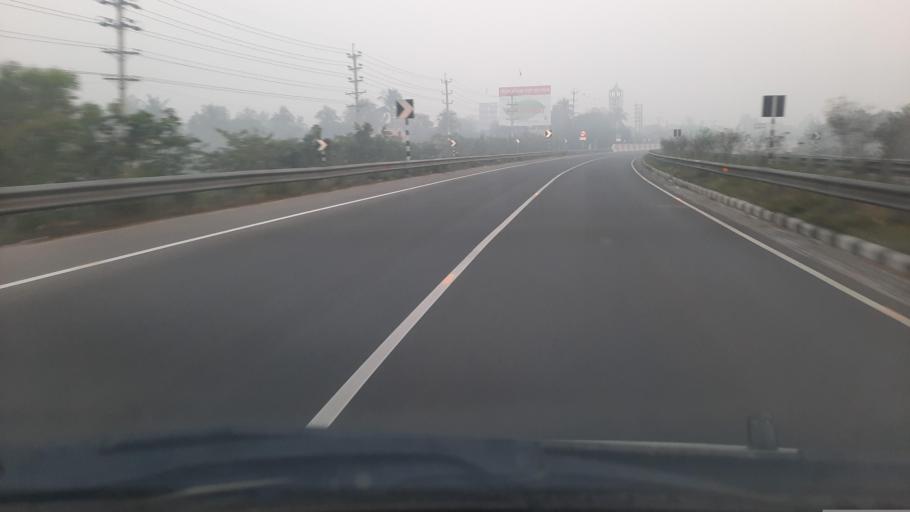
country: BD
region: Dhaka
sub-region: Dhaka
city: Dhaka
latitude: 23.6568
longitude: 90.3513
